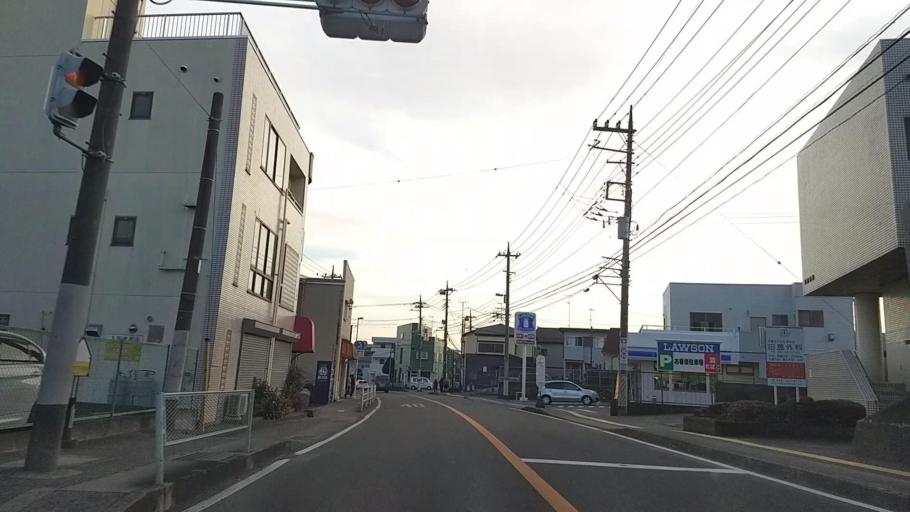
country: JP
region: Kanagawa
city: Atsugi
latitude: 35.4696
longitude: 139.3496
